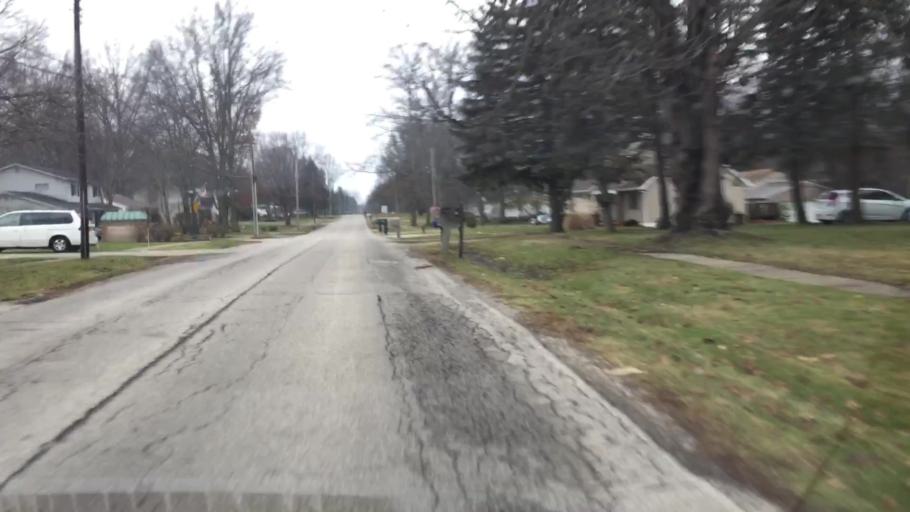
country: US
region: Ohio
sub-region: Summit County
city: Stow
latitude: 41.1825
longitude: -81.4340
